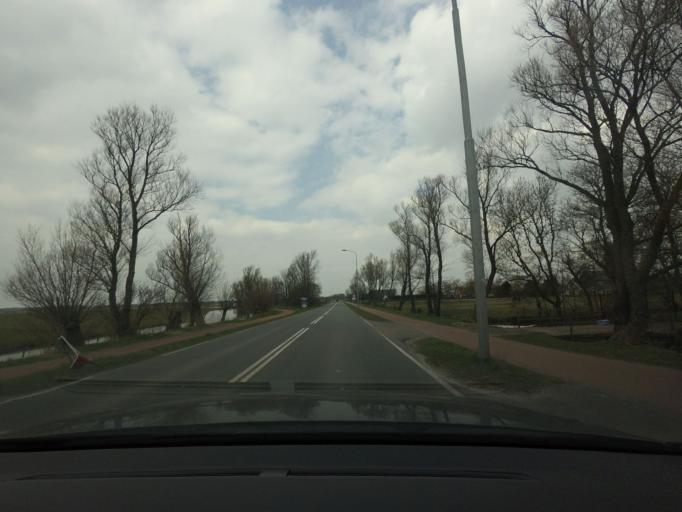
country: NL
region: North Holland
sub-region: Gemeente Alkmaar
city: Alkmaar
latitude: 52.6486
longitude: 4.7230
